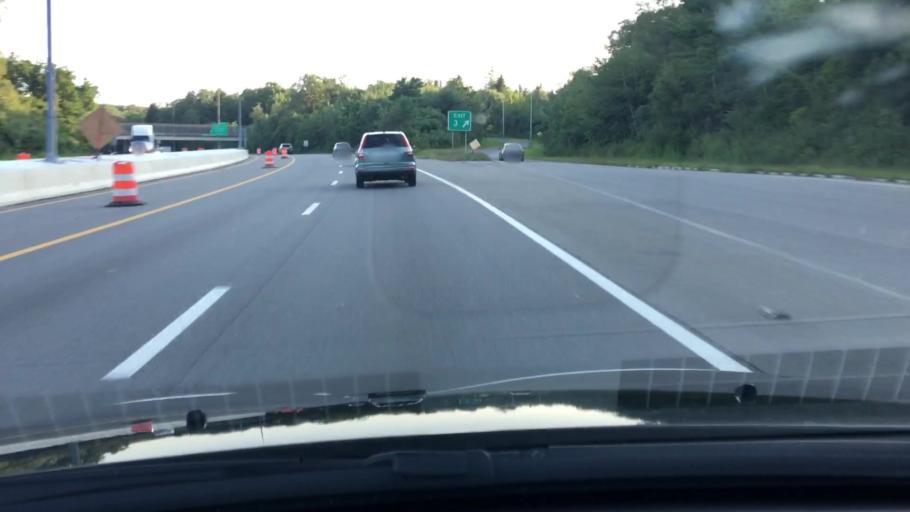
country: US
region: Massachusetts
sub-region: Worcester County
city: West Boylston
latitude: 42.3296
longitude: -71.8030
